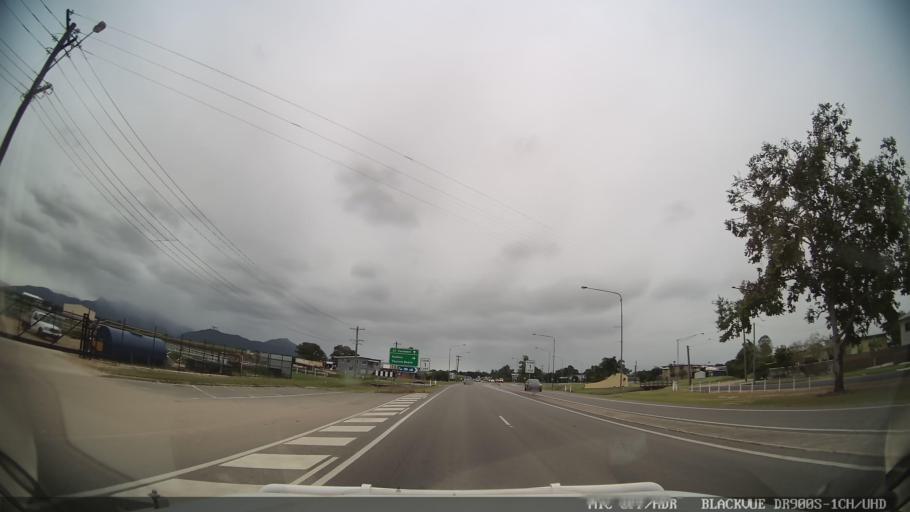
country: AU
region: Queensland
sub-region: Hinchinbrook
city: Ingham
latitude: -18.6425
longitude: 146.1631
